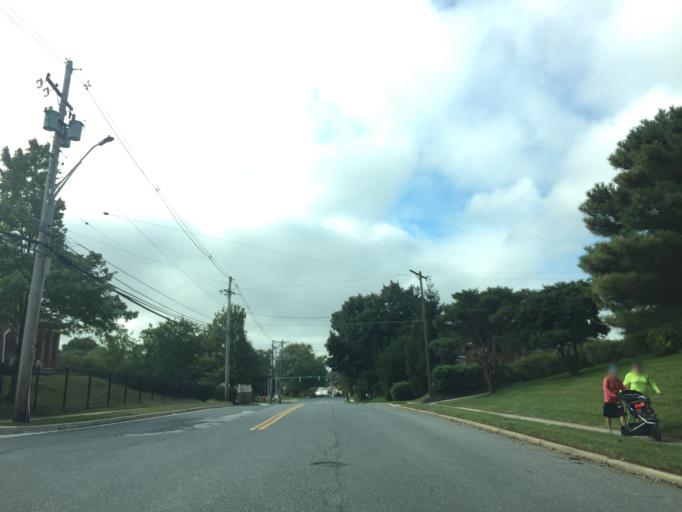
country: US
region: Maryland
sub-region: Baltimore County
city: Pikesville
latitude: 39.3767
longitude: -76.6771
